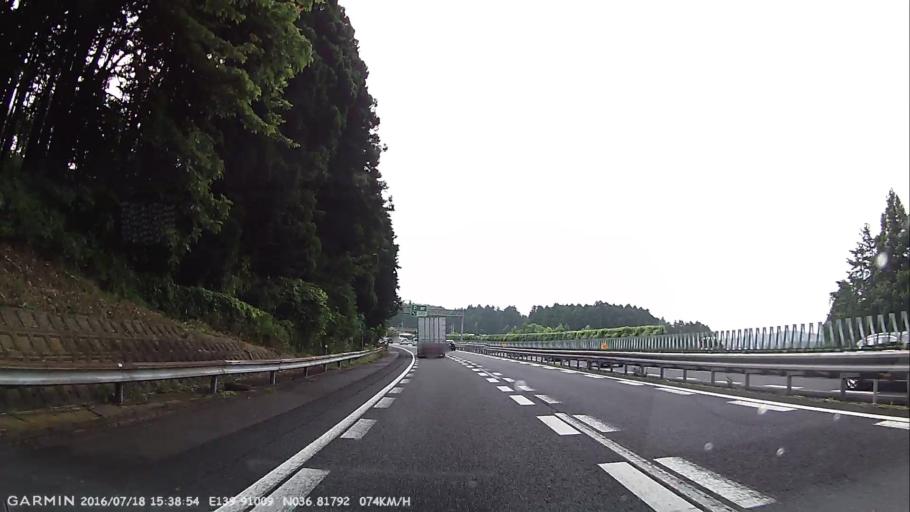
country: JP
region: Tochigi
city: Yaita
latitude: 36.8179
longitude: 139.9101
